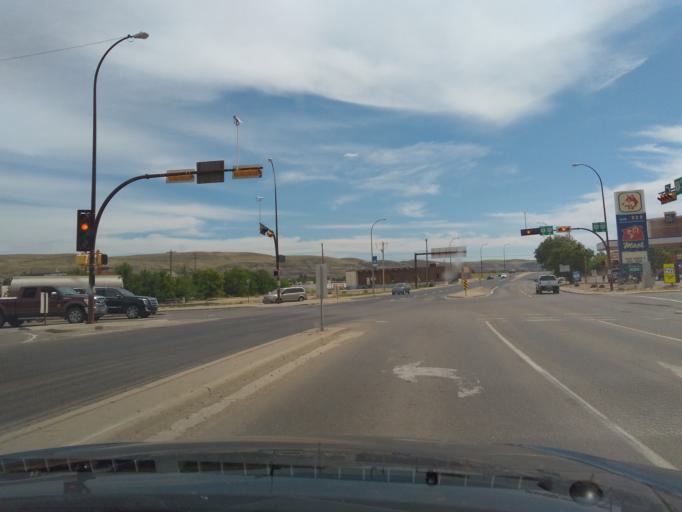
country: CA
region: Alberta
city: Three Hills
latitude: 51.4619
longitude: -112.7112
